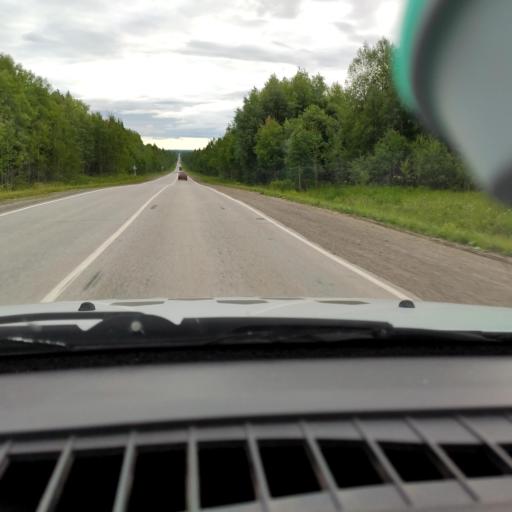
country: RU
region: Perm
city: Lys'va
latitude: 58.1342
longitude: 57.7344
